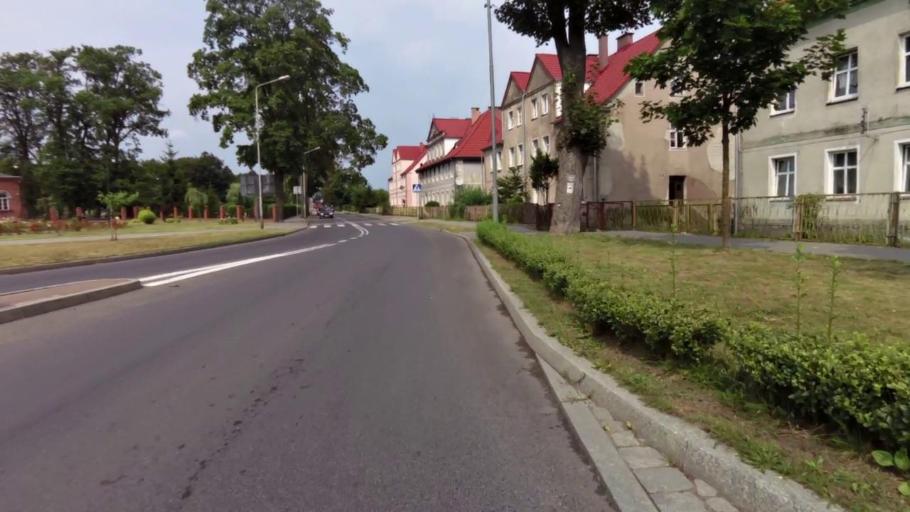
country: PL
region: West Pomeranian Voivodeship
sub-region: Powiat drawski
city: Drawsko Pomorskie
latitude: 53.5374
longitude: 15.8130
